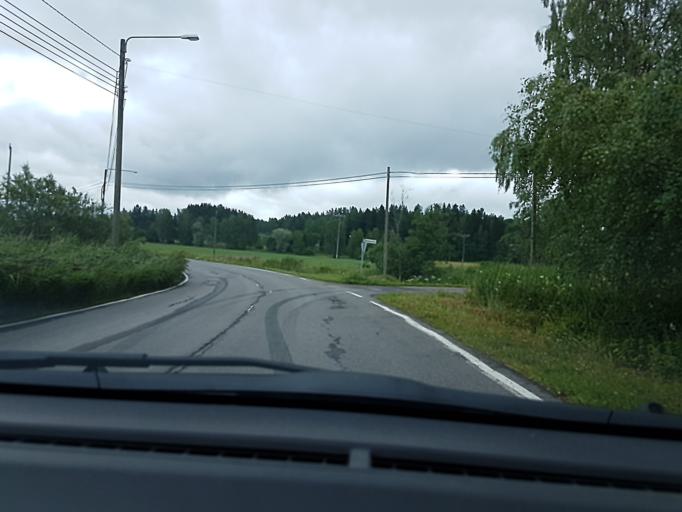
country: FI
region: Uusimaa
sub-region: Helsinki
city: Pornainen
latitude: 60.4351
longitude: 25.3854
